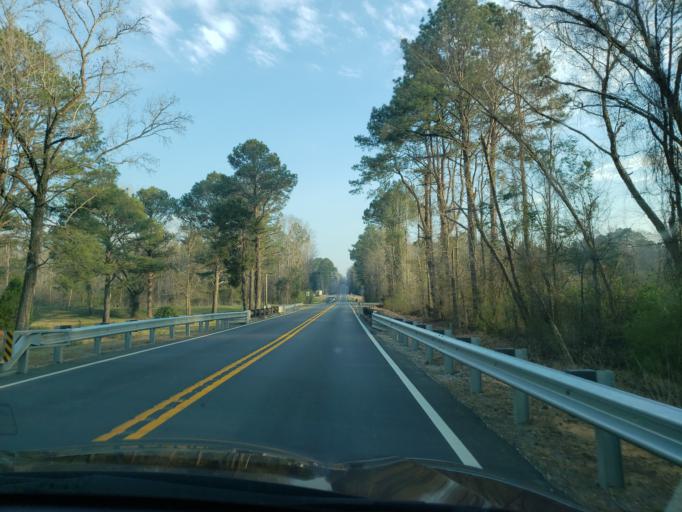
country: US
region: Alabama
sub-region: Hale County
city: Greensboro
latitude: 32.8213
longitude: -87.6006
